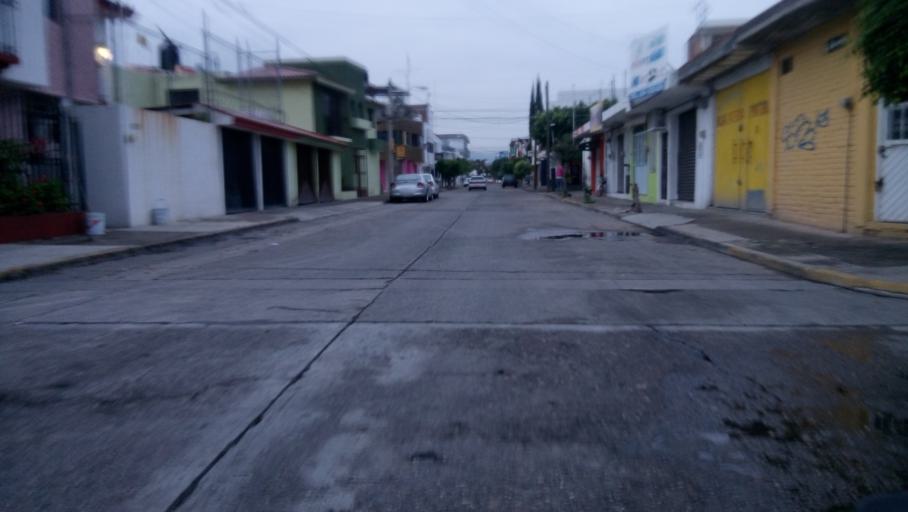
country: MX
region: Guanajuato
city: Leon
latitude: 21.1489
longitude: -101.6693
